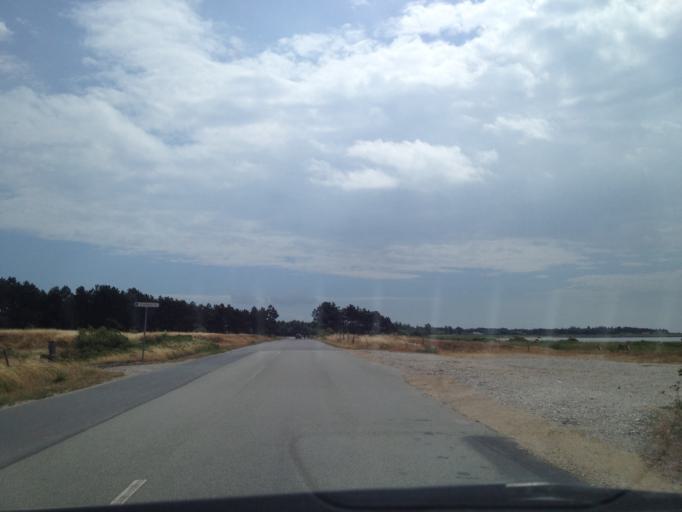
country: DK
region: Central Jutland
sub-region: Syddjurs Kommune
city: Ebeltoft
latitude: 56.1575
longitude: 10.6740
